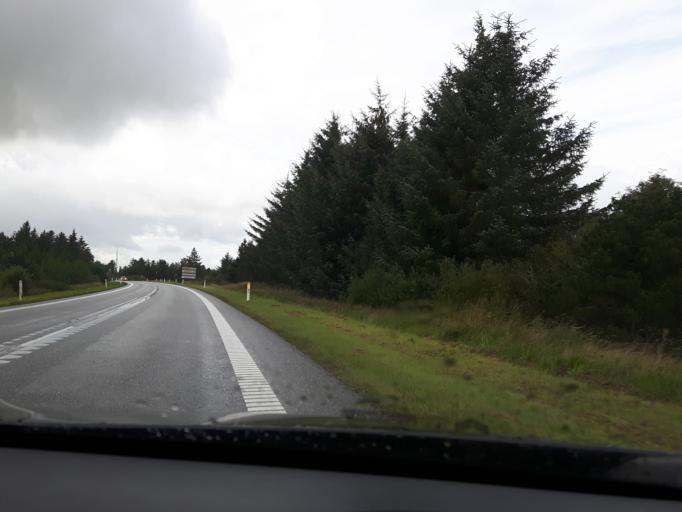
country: DK
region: North Denmark
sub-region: Jammerbugt Kommune
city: Fjerritslev
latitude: 57.0616
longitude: 9.1892
